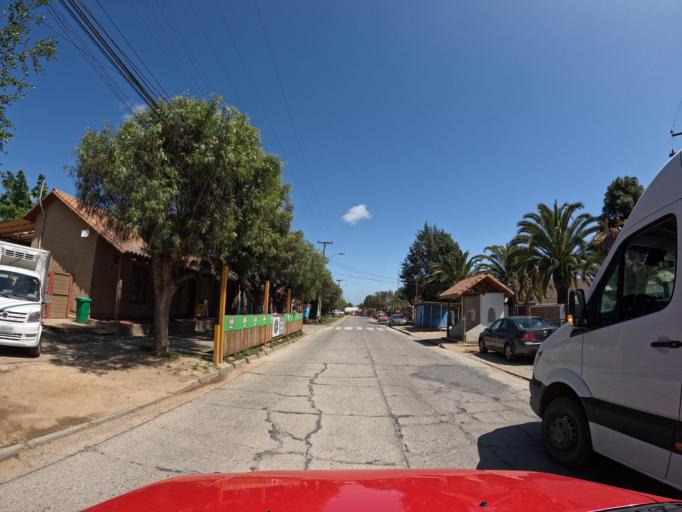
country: CL
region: O'Higgins
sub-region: Provincia de Colchagua
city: Santa Cruz
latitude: -34.7285
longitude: -71.6466
